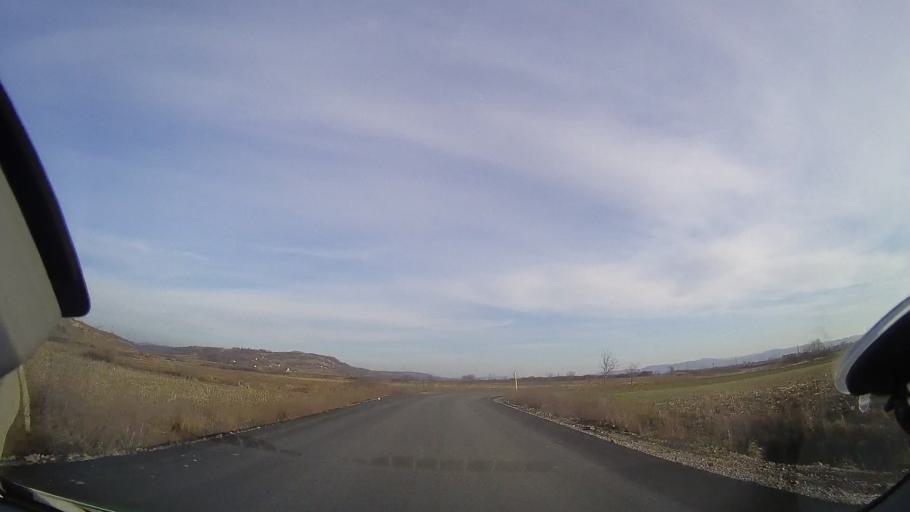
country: RO
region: Bihor
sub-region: Comuna Tileagd
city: Tileagd
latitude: 47.0865
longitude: 22.1812
